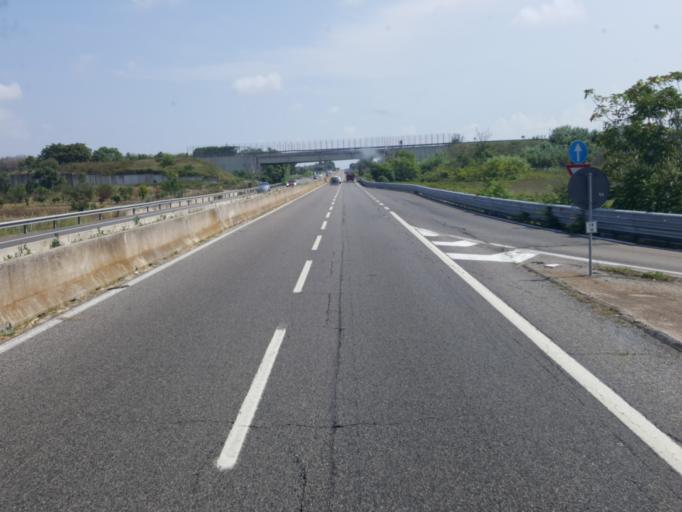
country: IT
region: Apulia
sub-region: Provincia di Brindisi
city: Torchiarolo
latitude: 40.4881
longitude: 18.0398
